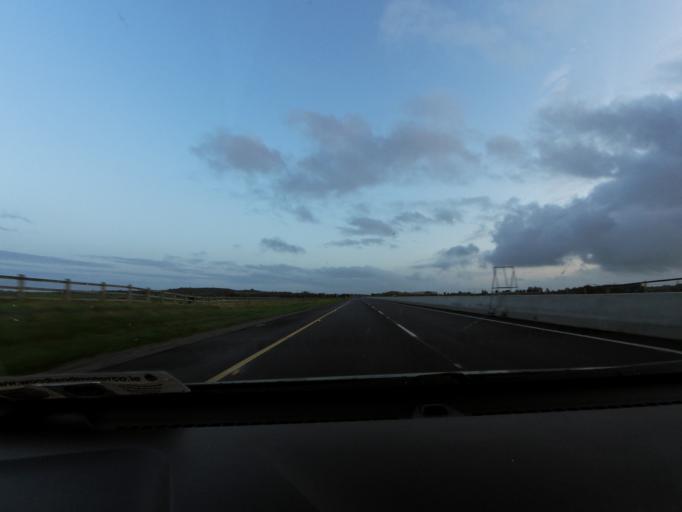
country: IE
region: Connaught
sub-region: County Galway
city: Athenry
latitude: 53.3755
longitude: -8.7944
